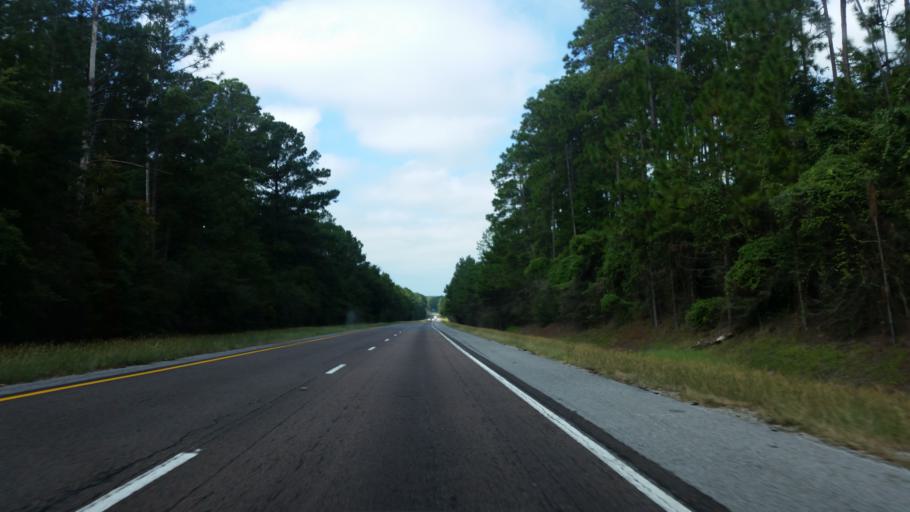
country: US
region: Alabama
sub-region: Baldwin County
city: Bay Minette
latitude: 30.9592
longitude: -87.7895
